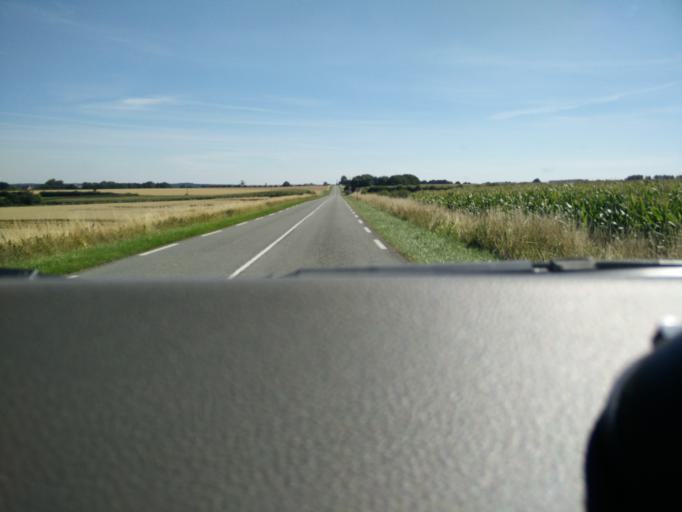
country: FR
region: Nord-Pas-de-Calais
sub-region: Departement du Nord
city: Sains-du-Nord
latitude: 50.1690
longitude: 4.0548
